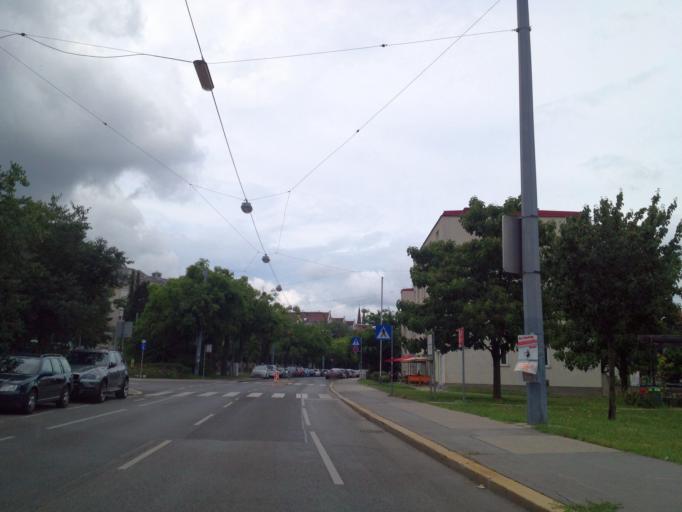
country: AT
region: Lower Austria
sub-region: Politischer Bezirk Modling
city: Perchtoldsdorf
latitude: 48.1690
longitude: 16.2797
